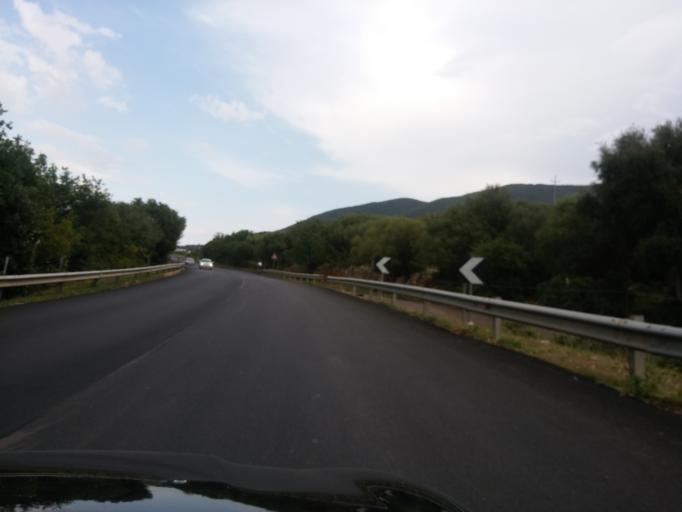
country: IT
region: Apulia
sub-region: Provincia di Foggia
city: Rignano Garganico
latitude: 41.7142
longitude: 15.5457
